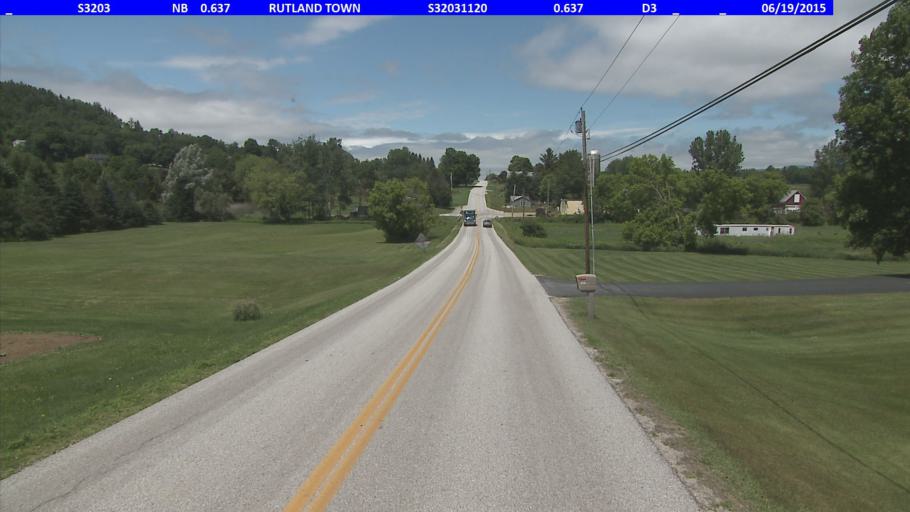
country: US
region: Vermont
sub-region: Rutland County
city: Rutland
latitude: 43.6623
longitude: -72.9996
